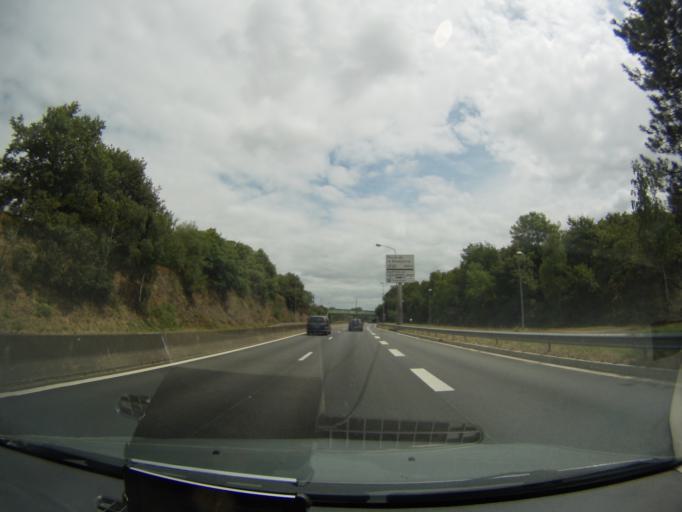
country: FR
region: Pays de la Loire
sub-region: Departement de la Loire-Atlantique
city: La Chapelle-sur-Erdre
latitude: 47.2570
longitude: -1.5449
